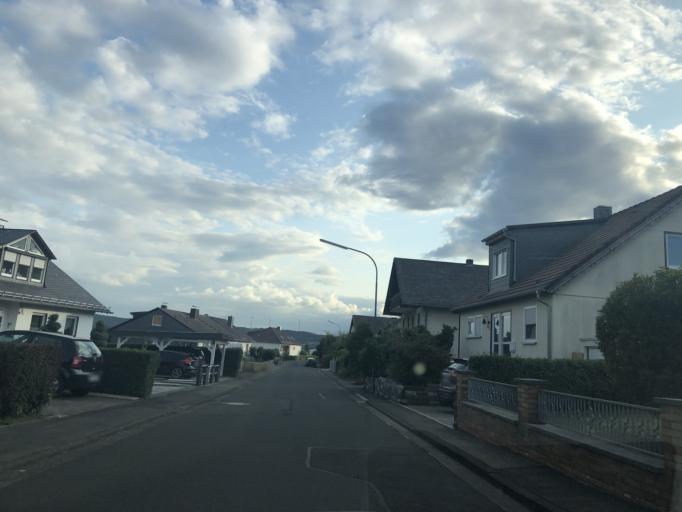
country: DE
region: Hesse
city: Amoneburg
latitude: 50.7942
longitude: 8.9288
